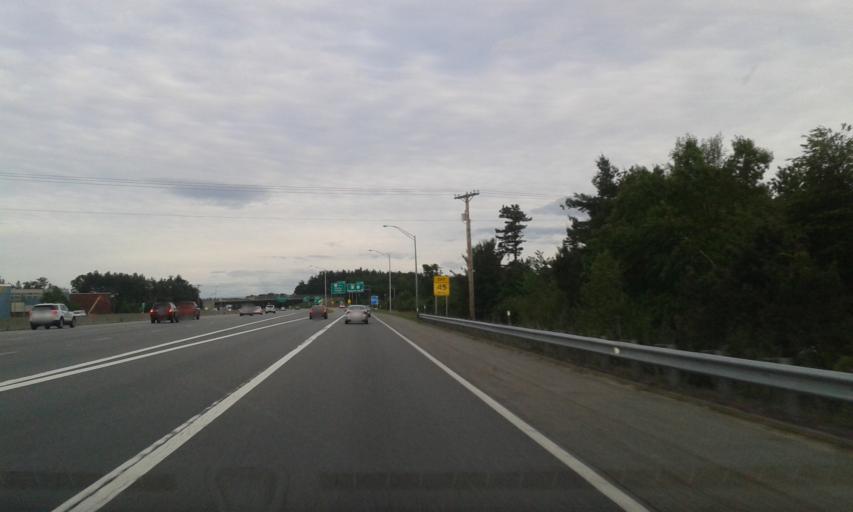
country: US
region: New Hampshire
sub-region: Hillsborough County
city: Nashua
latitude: 42.7526
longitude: -71.4933
